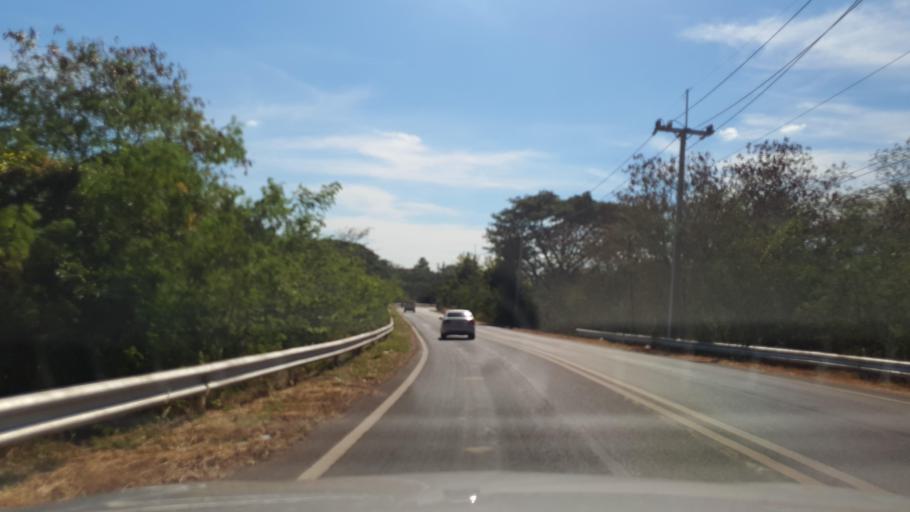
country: TH
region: Kalasin
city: Khao Wong
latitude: 16.7532
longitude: 104.1195
